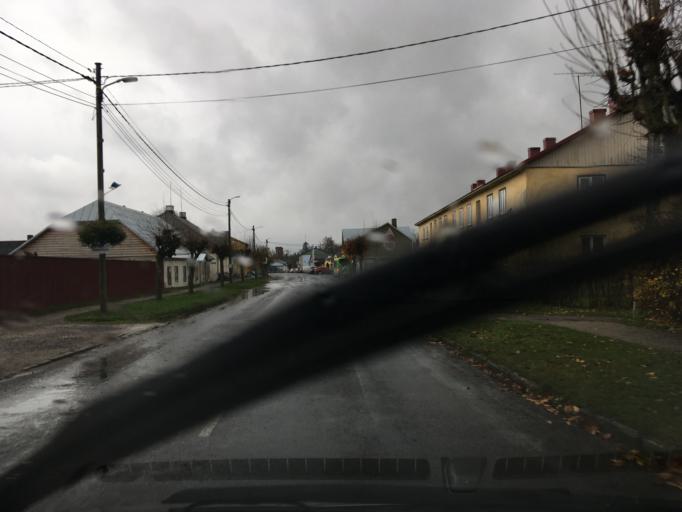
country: EE
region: Laeaene
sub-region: Lihula vald
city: Lihula
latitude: 58.6899
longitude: 23.8360
